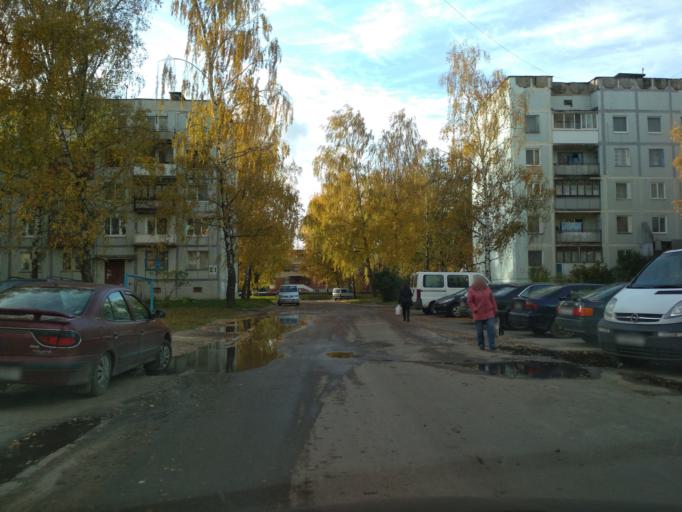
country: BY
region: Minsk
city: Mar''ina Horka
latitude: 53.5038
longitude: 28.1684
